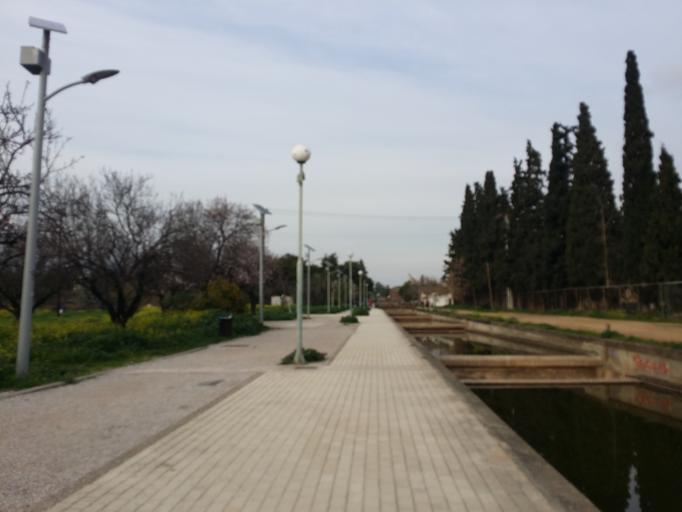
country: GR
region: Attica
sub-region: Nomarchia Athinas
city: Agioi Anargyroi
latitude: 38.0409
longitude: 23.7198
